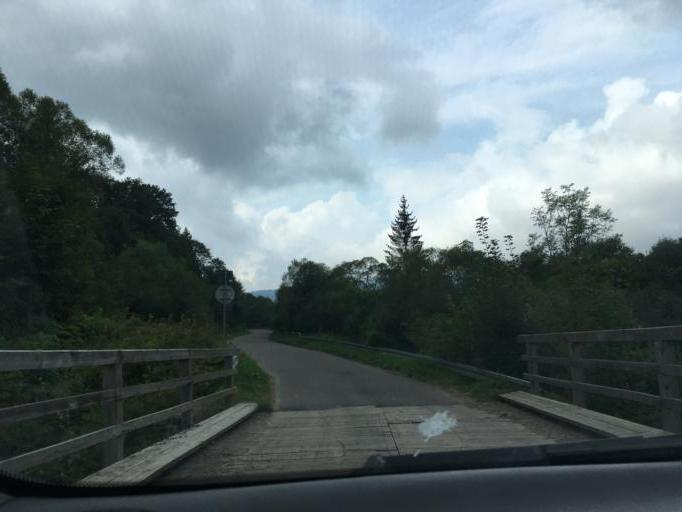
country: PL
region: Subcarpathian Voivodeship
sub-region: Powiat bieszczadzki
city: Lutowiska
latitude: 49.2185
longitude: 22.6325
